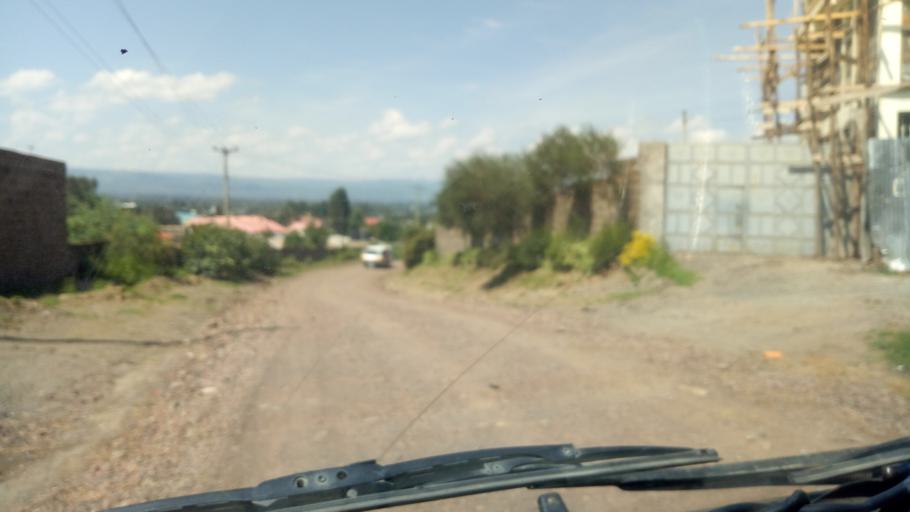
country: KE
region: Nakuru
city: Nakuru
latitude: -0.2766
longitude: 36.1091
